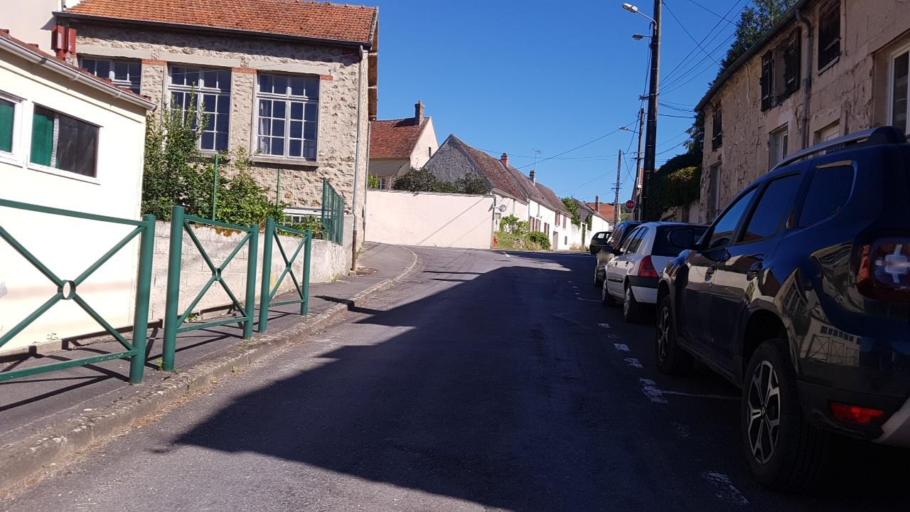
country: FR
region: Picardie
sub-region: Departement de l'Aisne
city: Chezy-sur-Marne
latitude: 49.0009
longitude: 3.3667
